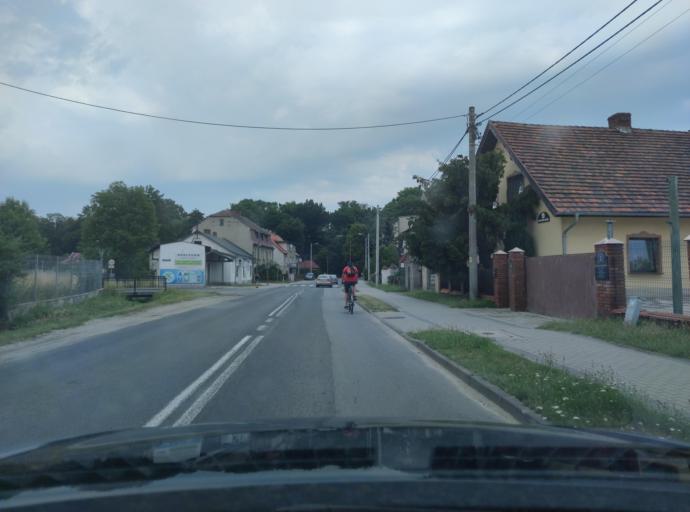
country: PL
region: Opole Voivodeship
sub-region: Powiat strzelecki
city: Strzelce Opolskie
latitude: 50.5065
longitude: 18.2962
